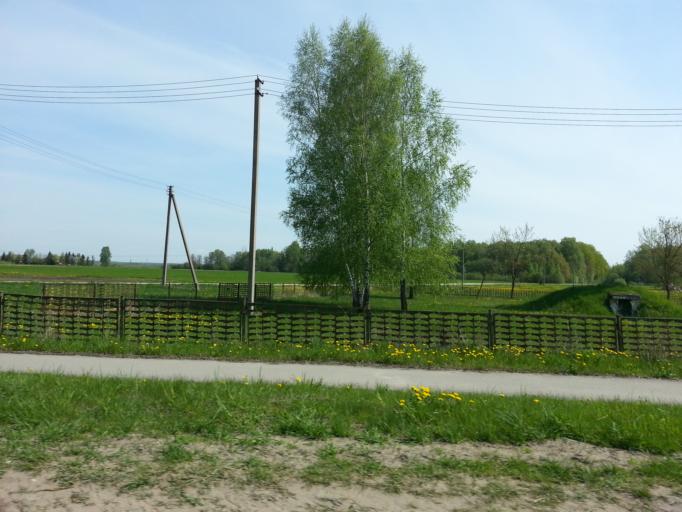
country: LT
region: Panevezys
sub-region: Panevezys City
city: Panevezys
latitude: 55.7743
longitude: 24.2931
